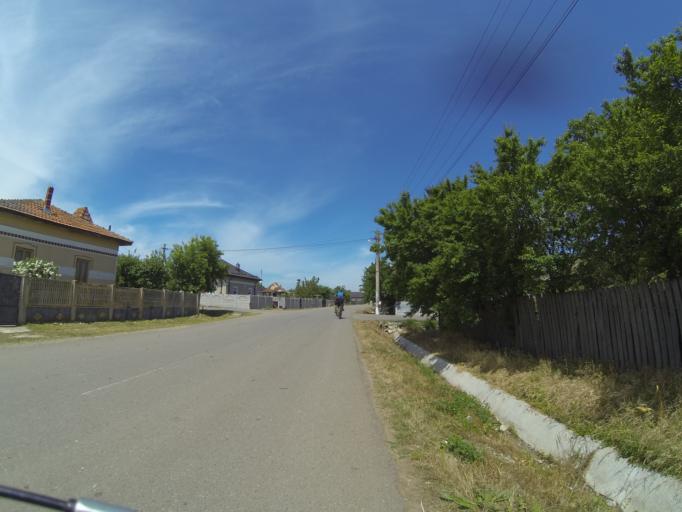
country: RO
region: Dolj
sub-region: Comuna Diosti
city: Radomir
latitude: 44.1585
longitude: 24.1628
